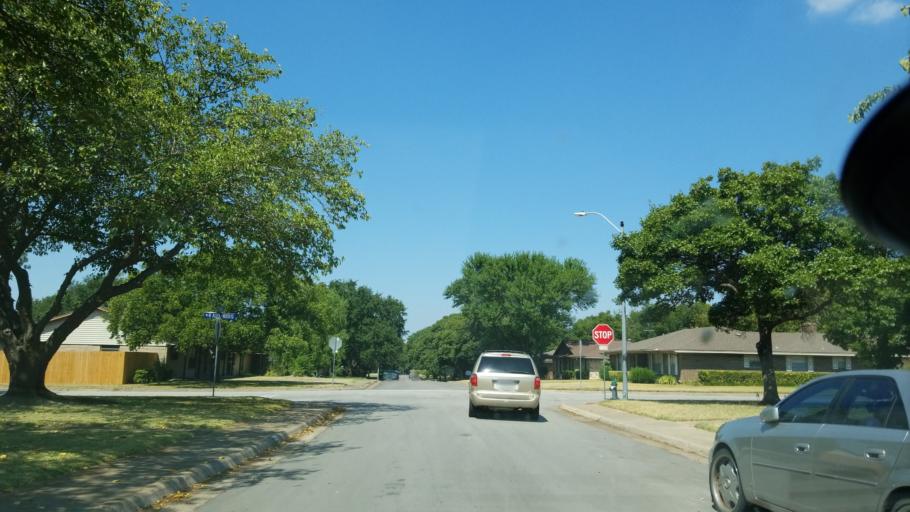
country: US
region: Texas
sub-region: Dallas County
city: Duncanville
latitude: 32.6542
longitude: -96.8949
